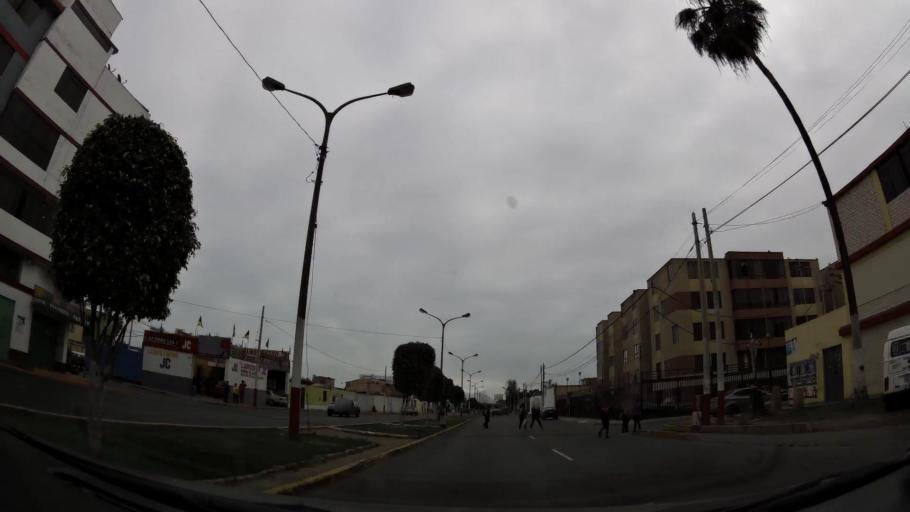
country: PE
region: Callao
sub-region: Callao
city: Callao
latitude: -12.0584
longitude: -77.1228
